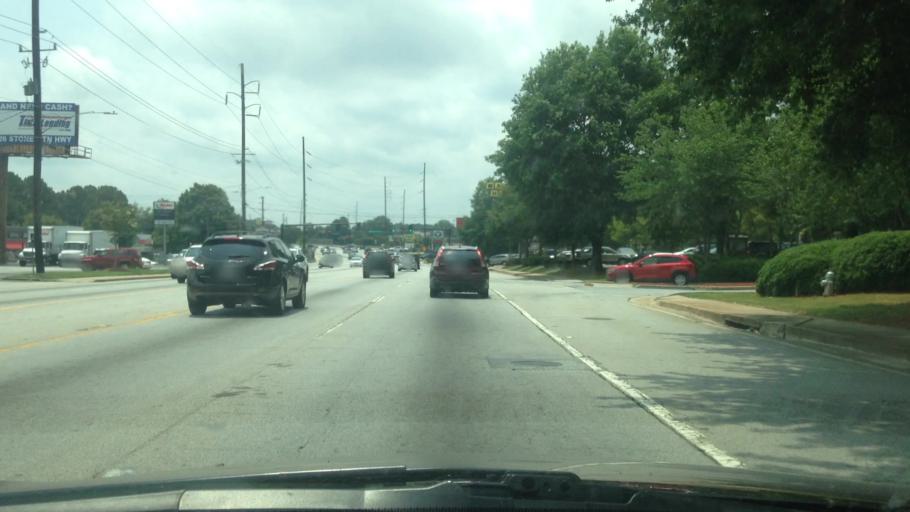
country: US
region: Georgia
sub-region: DeKalb County
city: Tucker
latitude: 33.8392
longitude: -84.2010
